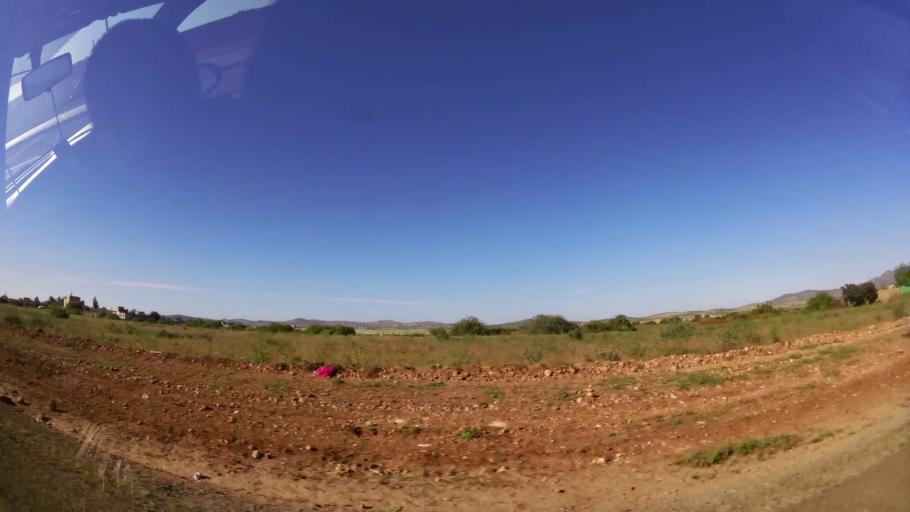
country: MA
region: Oriental
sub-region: Berkane-Taourirt
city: Ahfir
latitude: 35.0059
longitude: -2.1860
